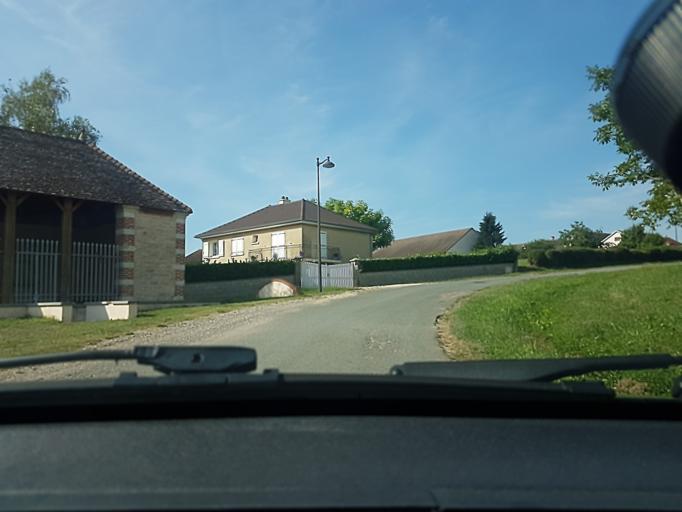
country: FR
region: Bourgogne
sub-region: Departement de Saone-et-Loire
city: Epervans
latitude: 46.7473
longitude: 4.9000
